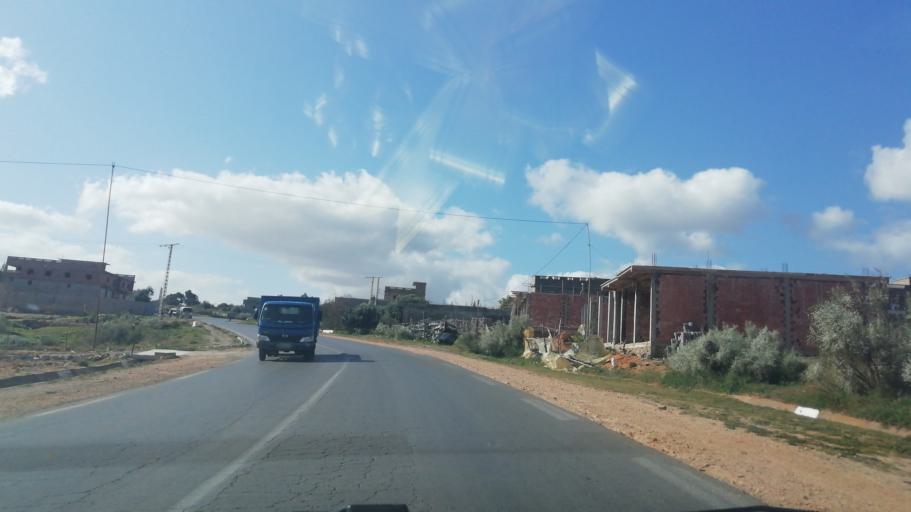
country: DZ
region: Relizane
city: Mazouna
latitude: 36.2879
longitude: 0.6473
